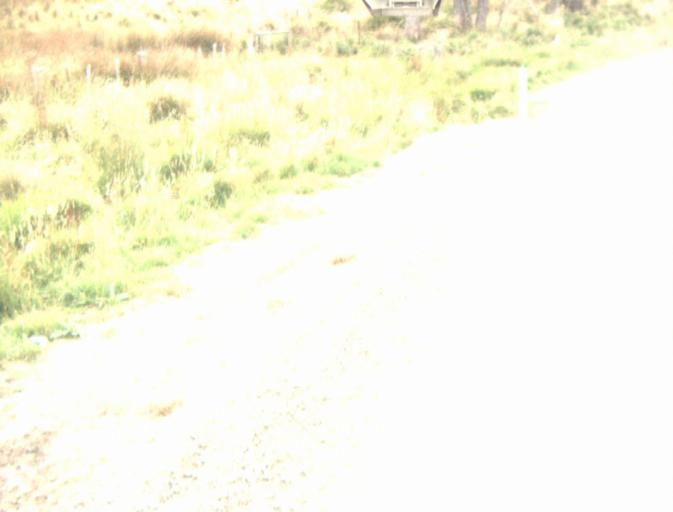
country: AU
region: Tasmania
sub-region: Northern Midlands
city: Evandale
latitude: -41.4575
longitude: 147.4624
